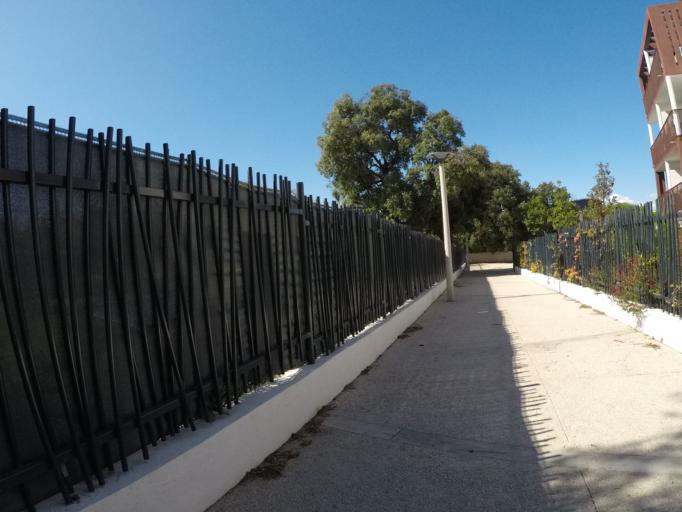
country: FR
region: Provence-Alpes-Cote d'Azur
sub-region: Departement des Bouches-du-Rhone
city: Marseille 09
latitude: 43.2386
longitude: 5.4025
